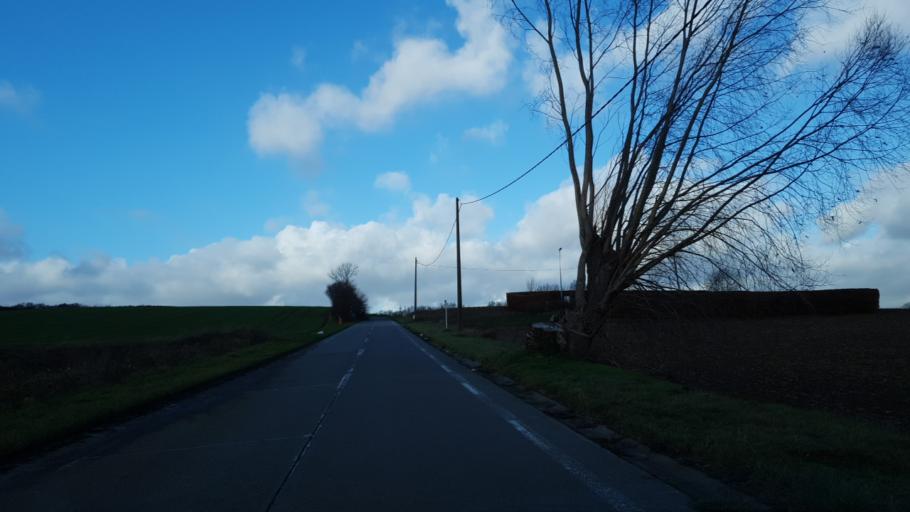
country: BE
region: Flanders
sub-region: Provincie Vlaams-Brabant
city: Kortenberg
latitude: 50.8608
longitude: 4.5815
